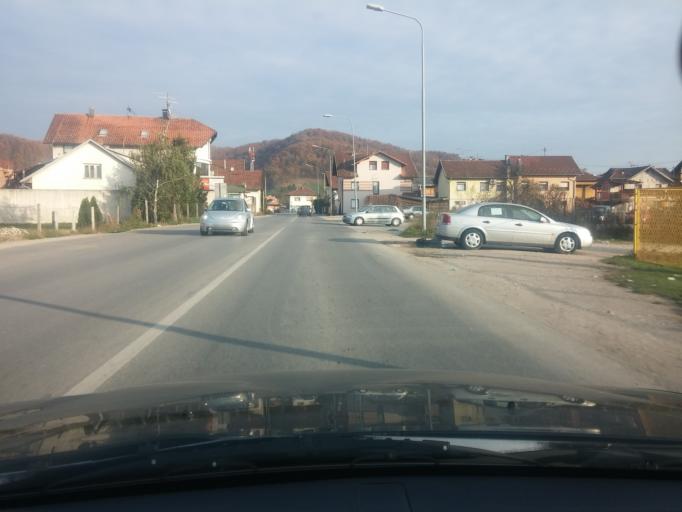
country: BA
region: Republika Srpska
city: Trn
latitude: 44.8177
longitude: 17.2122
